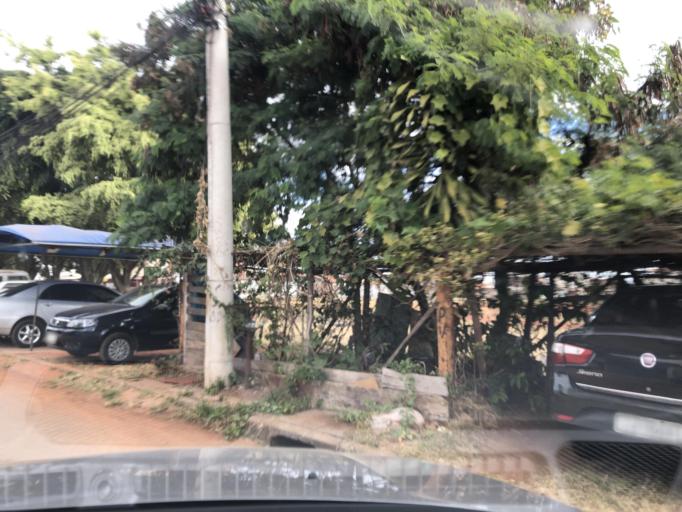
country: BR
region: Federal District
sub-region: Brasilia
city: Brasilia
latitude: -15.8879
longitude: -48.1043
